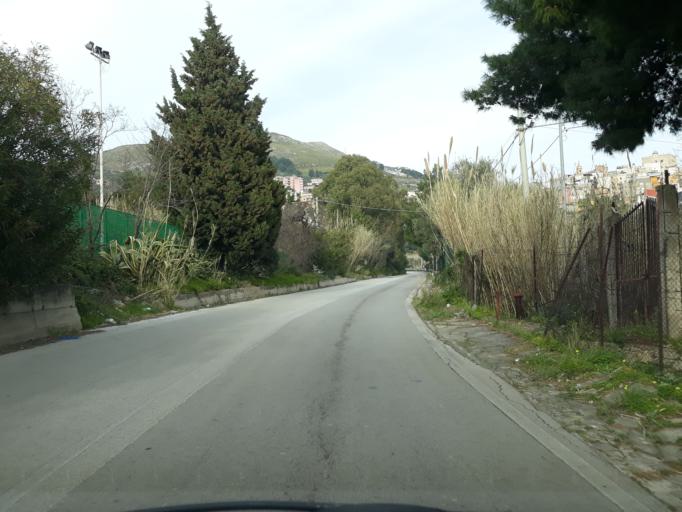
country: IT
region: Sicily
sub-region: Palermo
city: Giardinello
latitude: 38.0867
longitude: 13.1649
